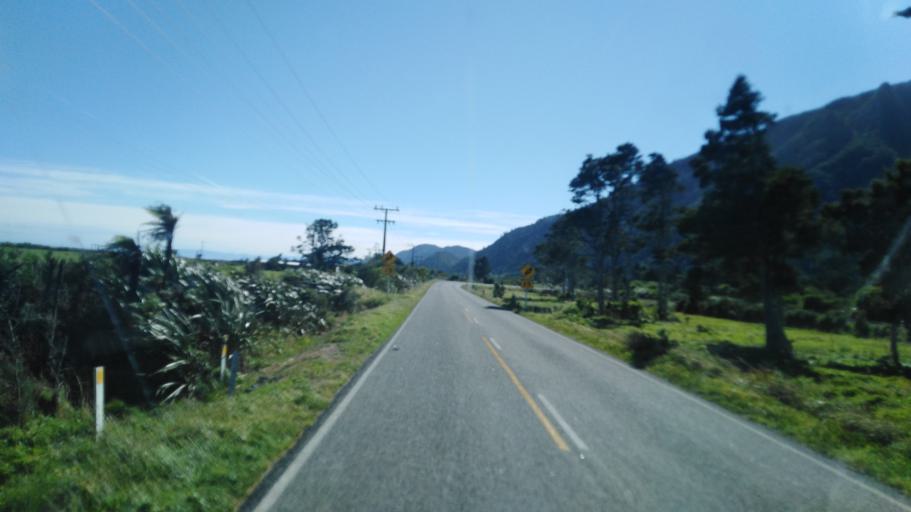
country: NZ
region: West Coast
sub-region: Buller District
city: Westport
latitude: -41.6523
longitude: 171.8278
